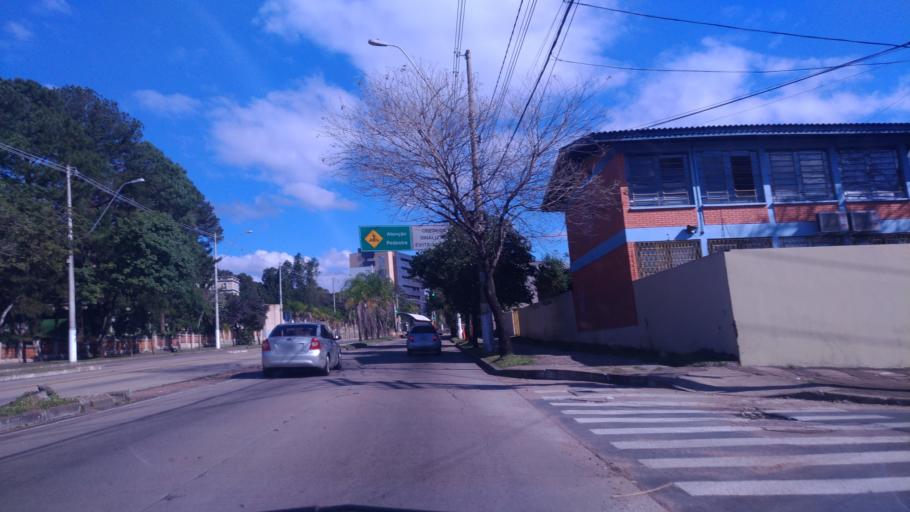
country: BR
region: Rio Grande do Sul
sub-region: Porto Alegre
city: Porto Alegre
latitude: -30.0694
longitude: -51.1887
